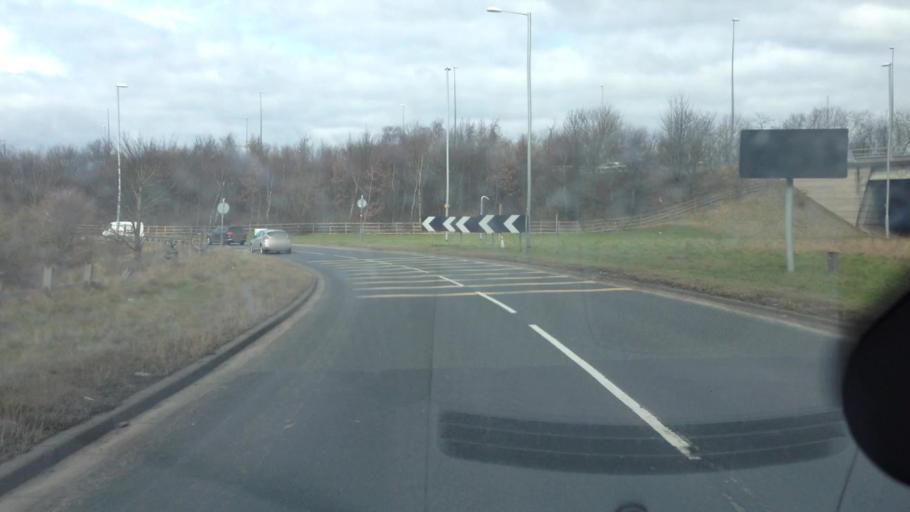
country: GB
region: England
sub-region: City and Borough of Leeds
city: Leeds
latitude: 53.7676
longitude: -1.5164
